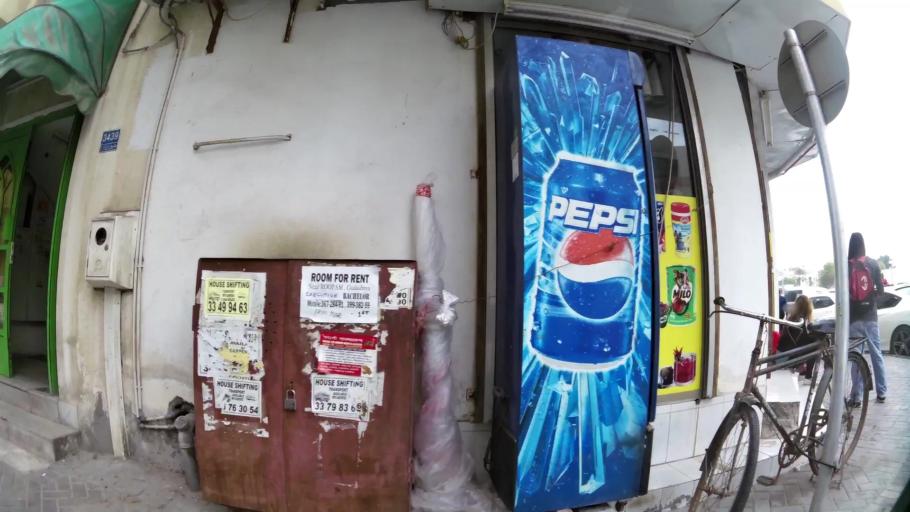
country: BH
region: Manama
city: Manama
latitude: 26.2244
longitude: 50.5887
